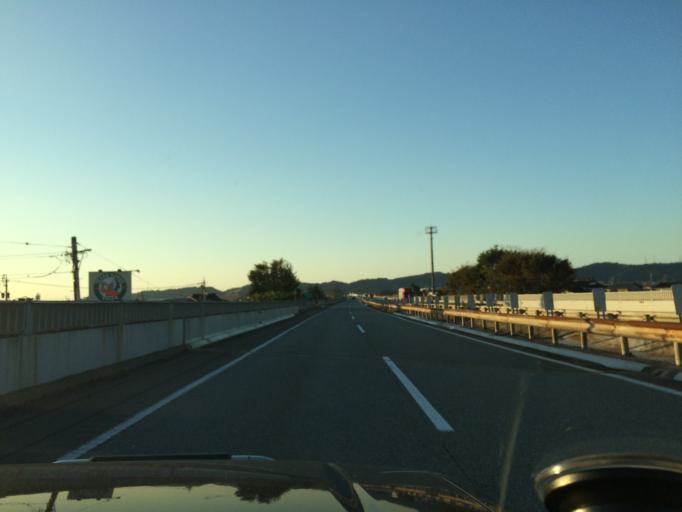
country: JP
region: Toyama
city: Toyama-shi
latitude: 36.6670
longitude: 137.1840
